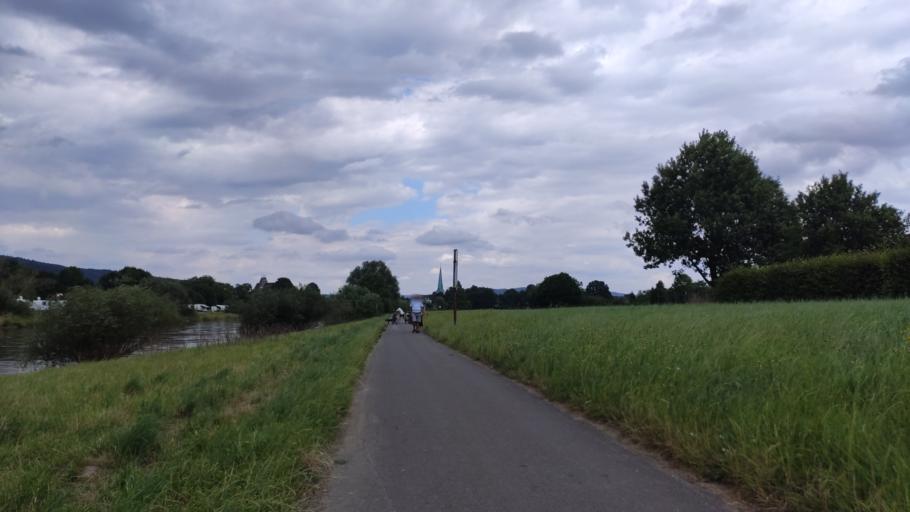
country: DE
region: Lower Saxony
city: Holzminden
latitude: 51.8217
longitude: 9.4378
